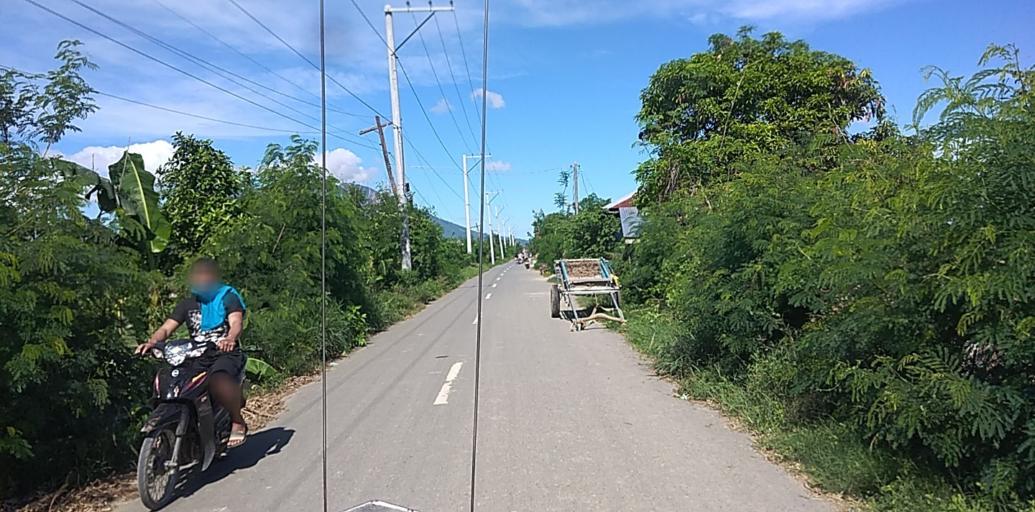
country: PH
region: Central Luzon
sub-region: Province of Pampanga
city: Candating
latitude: 15.1295
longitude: 120.8089
